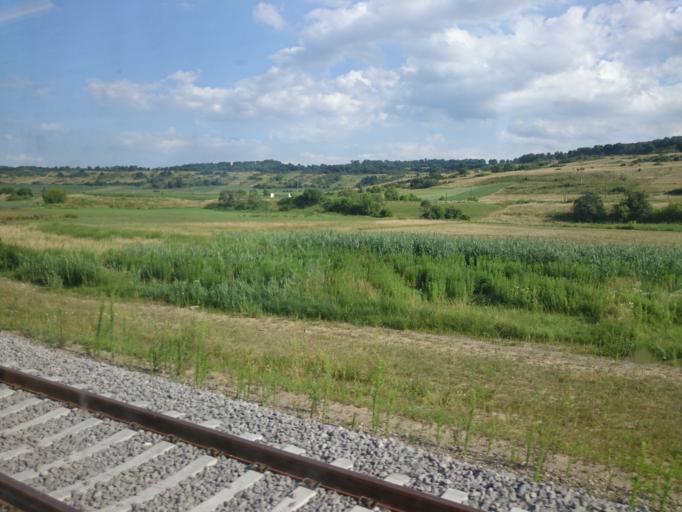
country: RO
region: Sibiu
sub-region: Comuna Laslea
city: Laslea
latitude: 46.2205
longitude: 24.6341
